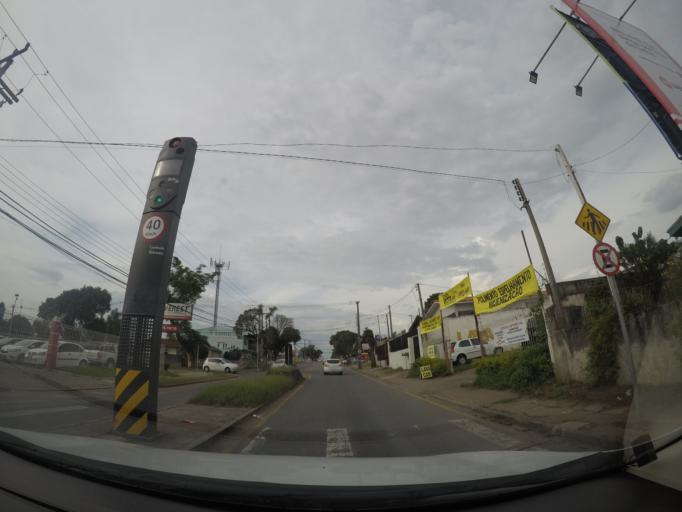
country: BR
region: Parana
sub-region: Sao Jose Dos Pinhais
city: Sao Jose dos Pinhais
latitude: -25.5015
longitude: -49.2547
